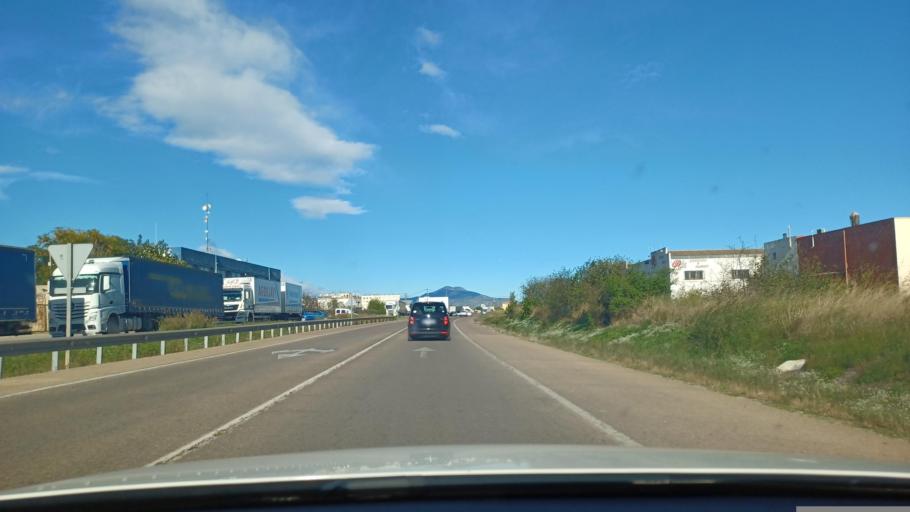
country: ES
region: Valencia
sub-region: Provincia de Castello
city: Vinaros
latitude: 40.4724
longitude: 0.4656
